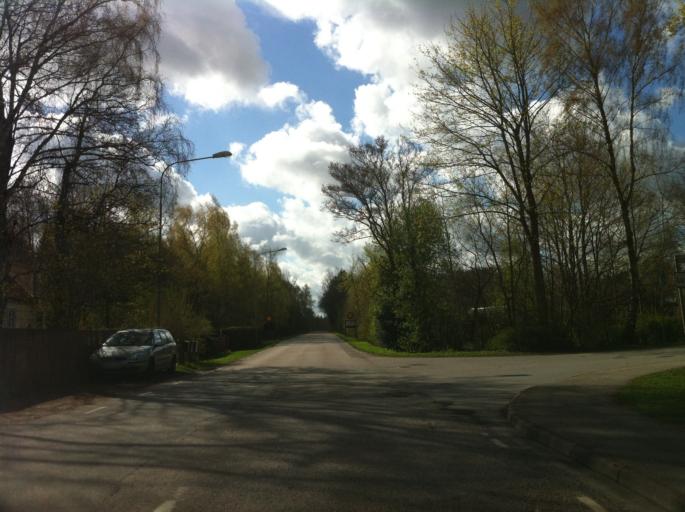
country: SE
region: Skane
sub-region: Hoors Kommun
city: Satofta
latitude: 55.9006
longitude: 13.6091
